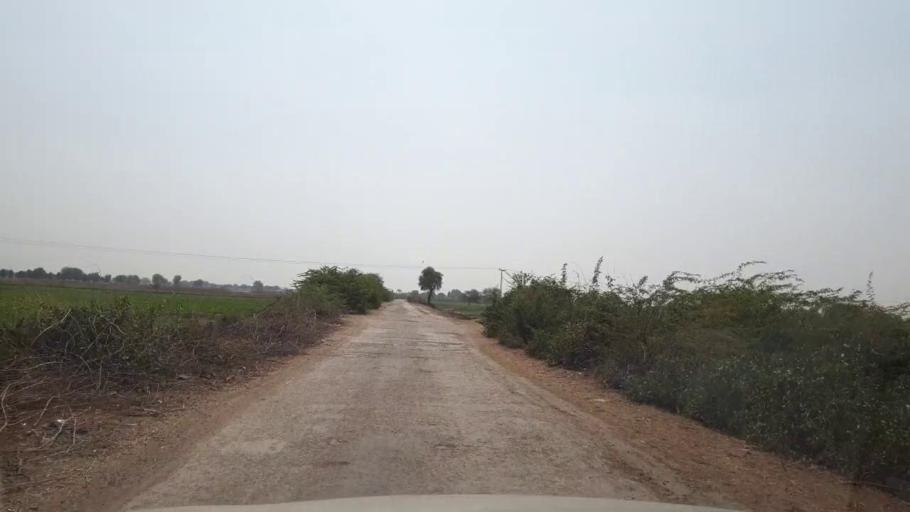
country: PK
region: Sindh
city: Dhoro Naro
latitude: 25.4727
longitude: 69.6382
